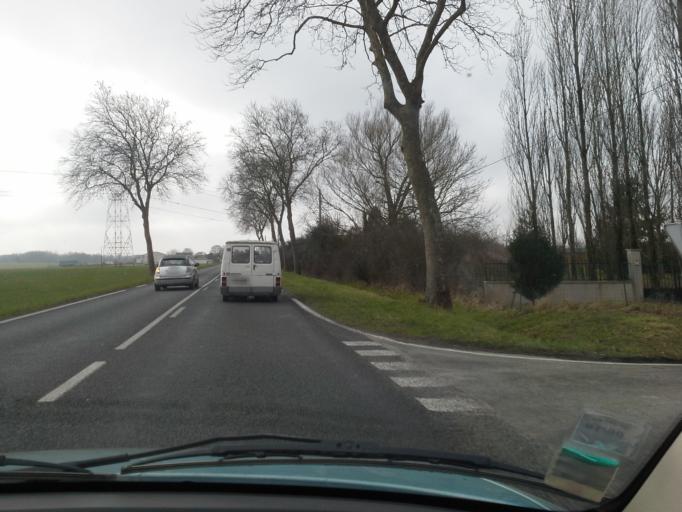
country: FR
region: Centre
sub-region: Departement d'Indre-et-Loire
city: Villedomer
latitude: 47.5607
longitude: 0.8755
